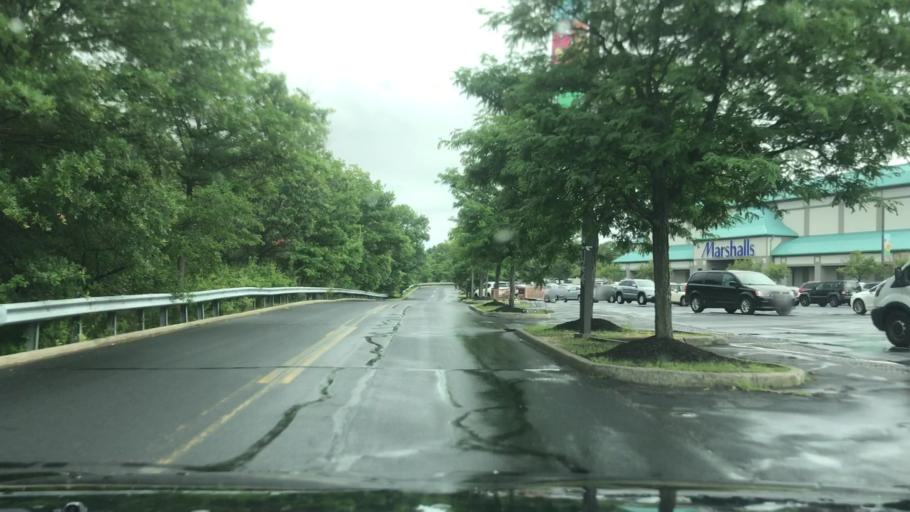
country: US
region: New Jersey
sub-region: Ocean County
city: Toms River
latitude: 39.9764
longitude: -74.1805
